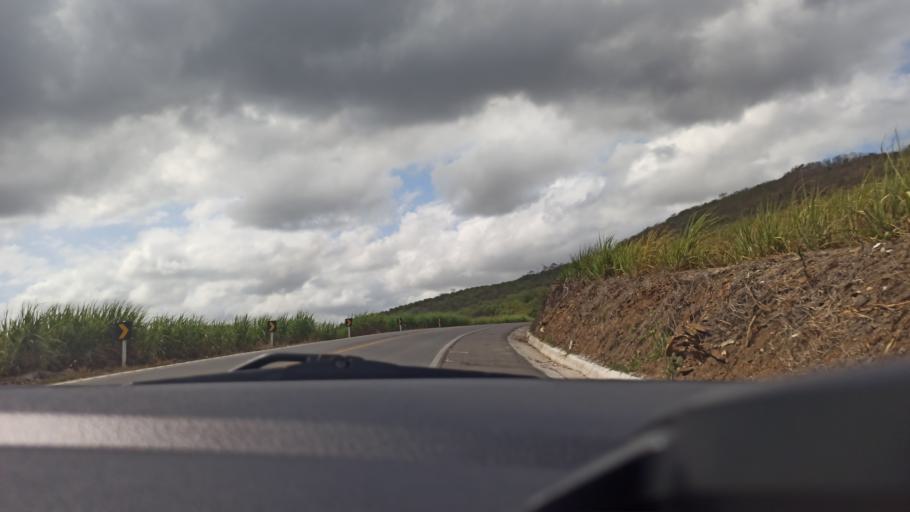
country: BR
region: Pernambuco
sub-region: Timbauba
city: Timbauba
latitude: -7.5280
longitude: -35.2896
